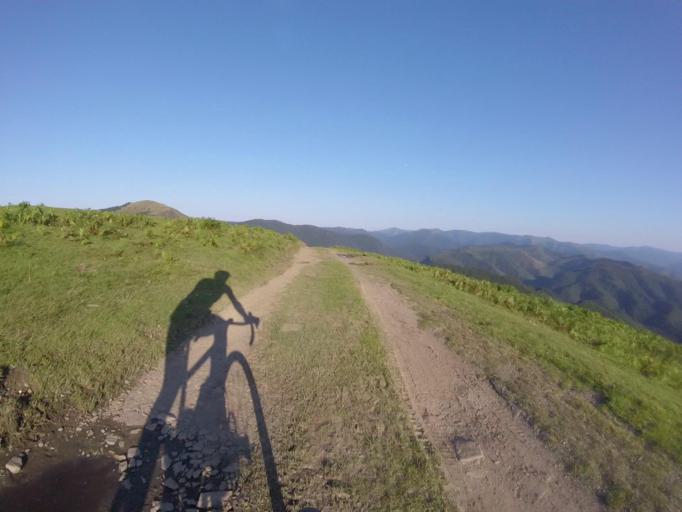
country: ES
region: Navarre
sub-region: Provincia de Navarra
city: Arano
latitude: 43.2430
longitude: -1.8472
